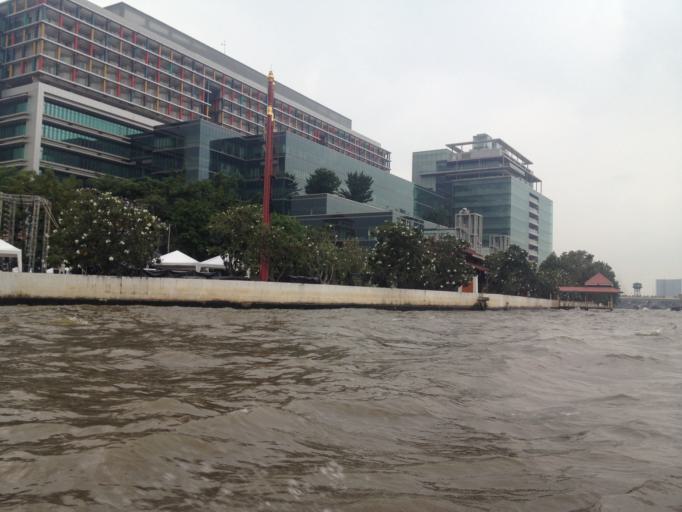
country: TH
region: Bangkok
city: Bangkok Noi
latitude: 13.7608
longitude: 100.4876
